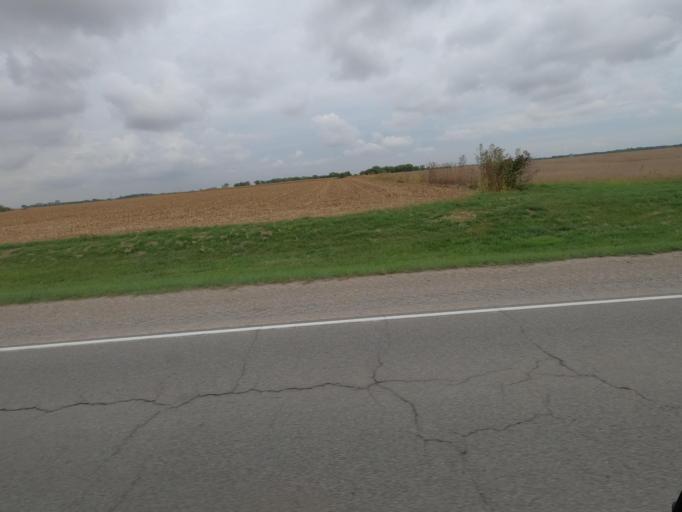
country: US
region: Iowa
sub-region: Wapello County
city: Ottumwa
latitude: 40.9683
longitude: -92.2365
